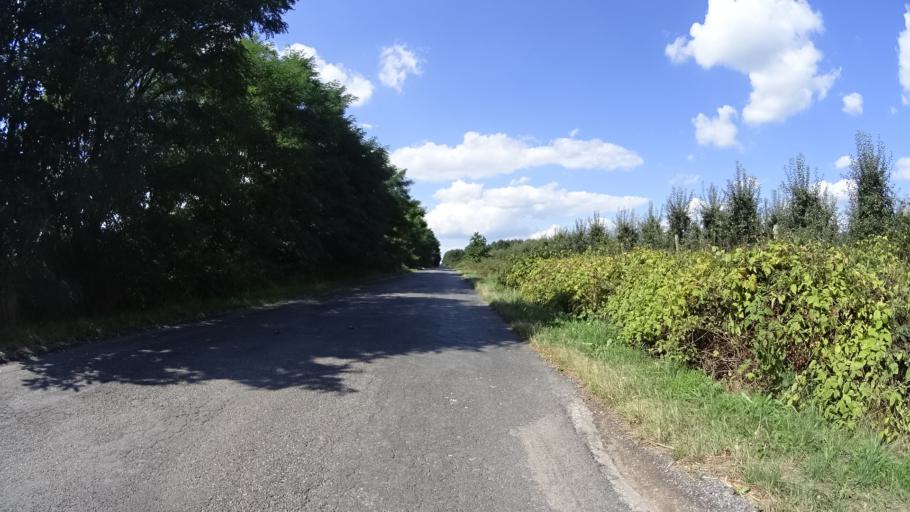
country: PL
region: Masovian Voivodeship
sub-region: Powiat grojecki
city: Mogielnica
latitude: 51.6832
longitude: 20.7599
